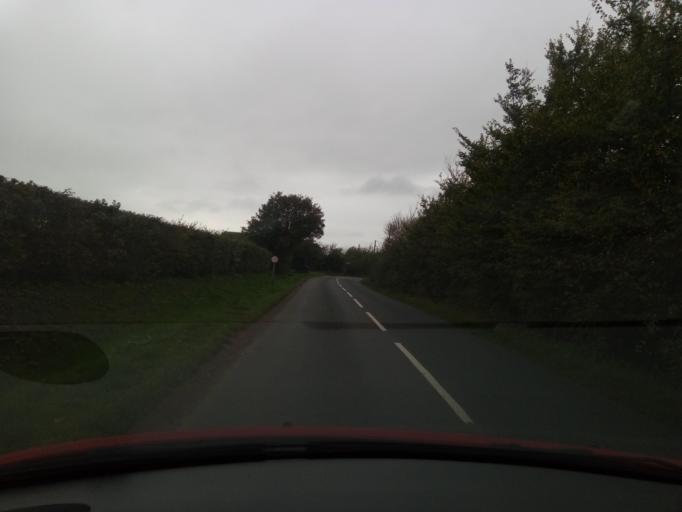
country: GB
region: England
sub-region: Essex
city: Brightlingsea
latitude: 51.7928
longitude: 0.9814
